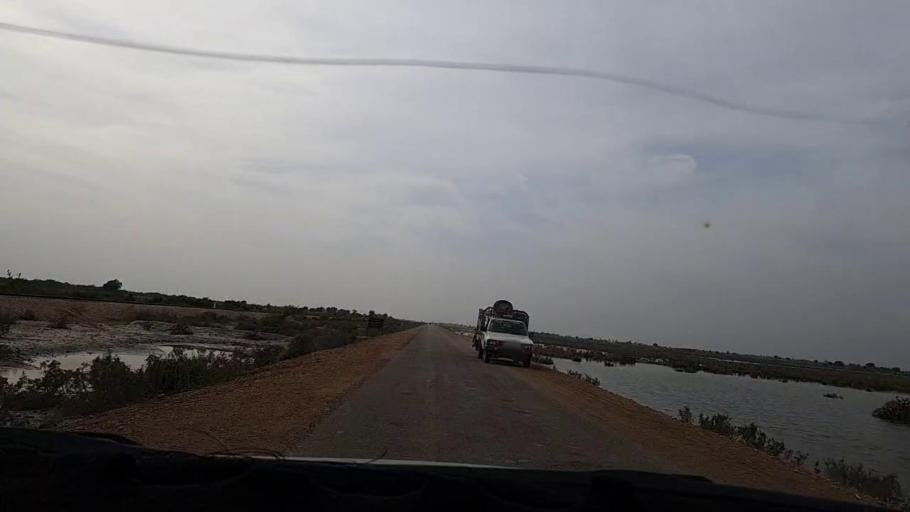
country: PK
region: Sindh
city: Pithoro
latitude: 25.5157
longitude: 69.2902
